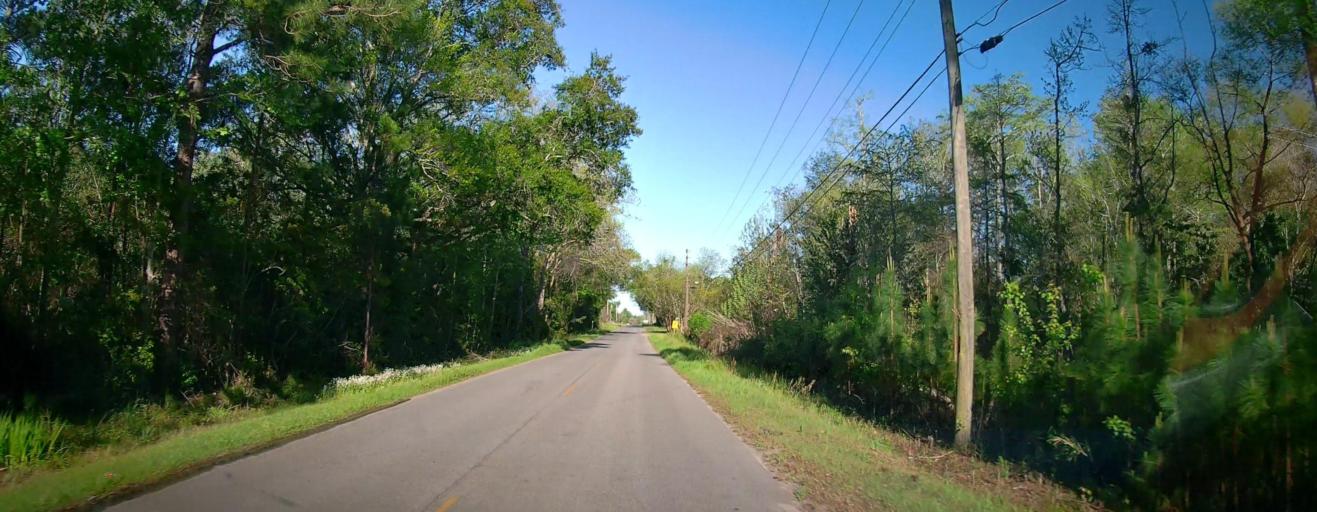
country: US
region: Georgia
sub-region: Ben Hill County
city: Fitzgerald
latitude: 31.7288
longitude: -83.2765
